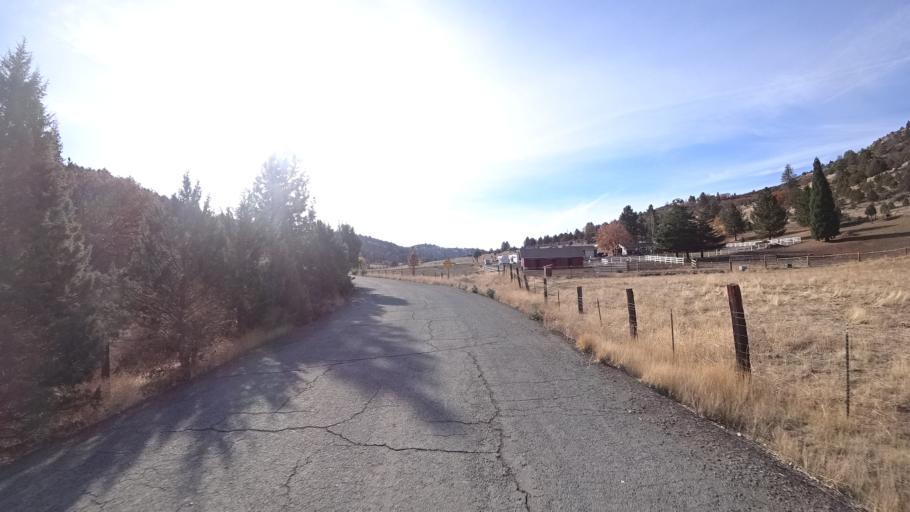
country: US
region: California
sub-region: Siskiyou County
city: Montague
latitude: 41.5981
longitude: -122.5774
